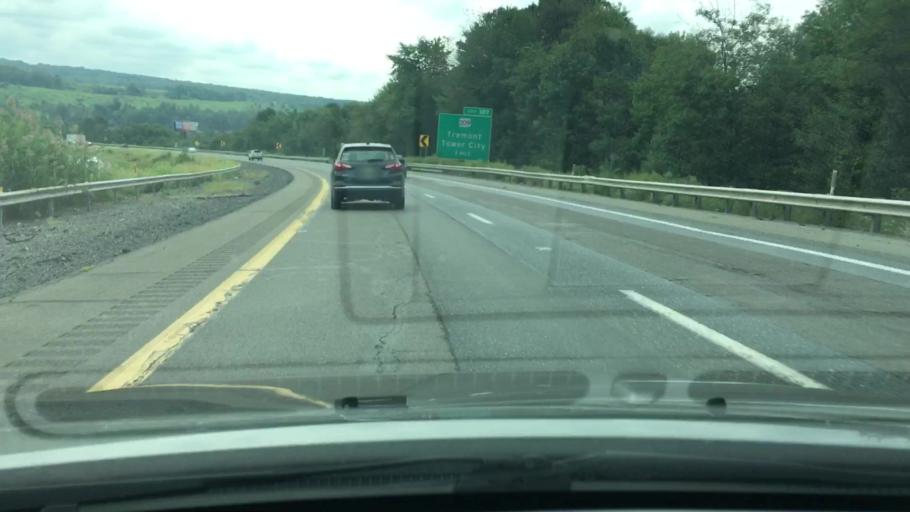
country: US
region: Pennsylvania
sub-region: Schuylkill County
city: Tremont
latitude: 40.6333
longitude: -76.4453
